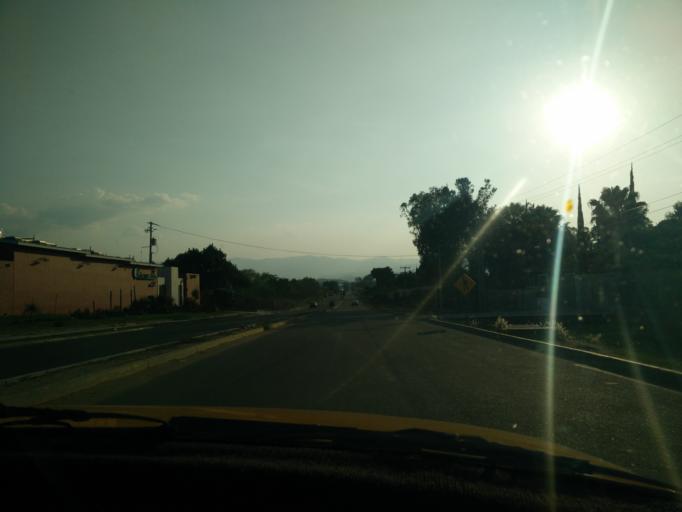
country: MX
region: Oaxaca
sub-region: San Lorenzo Cacaotepec
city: Santiago Etla
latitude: 17.1364
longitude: -96.7754
